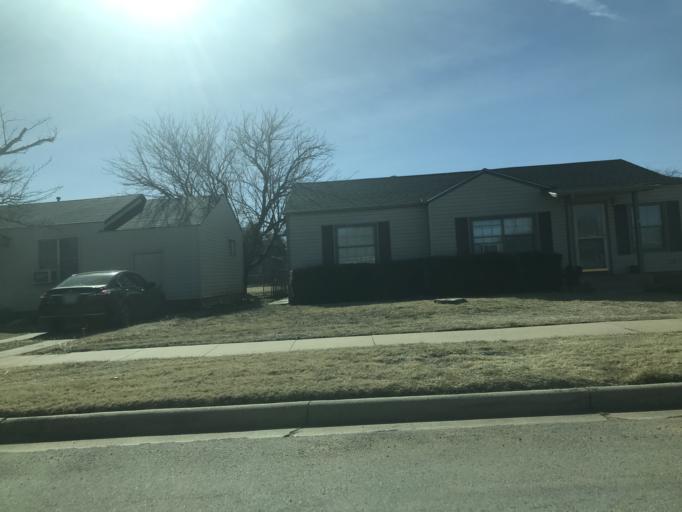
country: US
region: Texas
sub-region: Taylor County
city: Abilene
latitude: 32.4775
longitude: -99.7434
